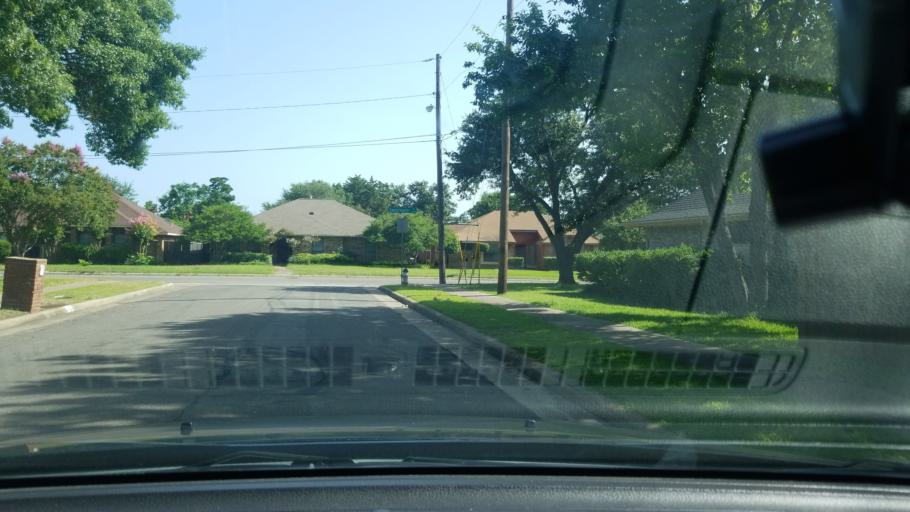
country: US
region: Texas
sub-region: Dallas County
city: Highland Park
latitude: 32.8102
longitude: -96.6928
